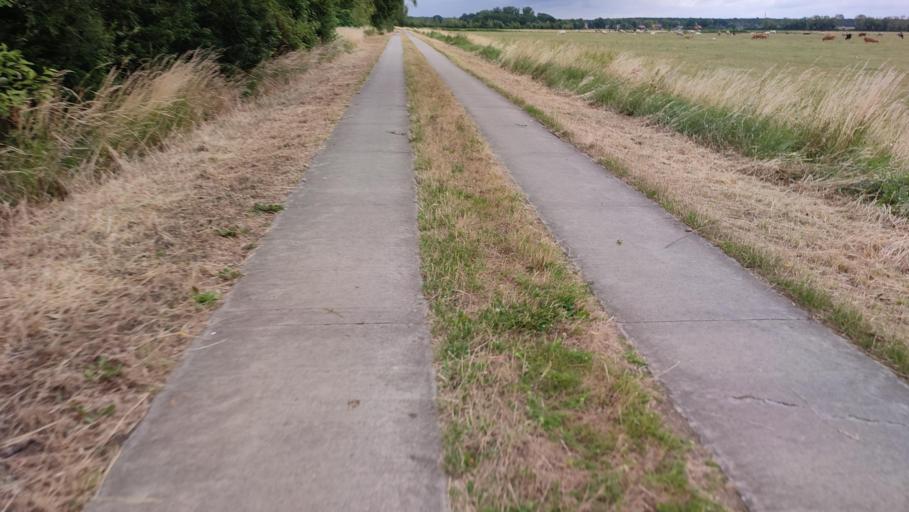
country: DE
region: Lower Saxony
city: Hitzacker
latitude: 53.1692
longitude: 11.1026
